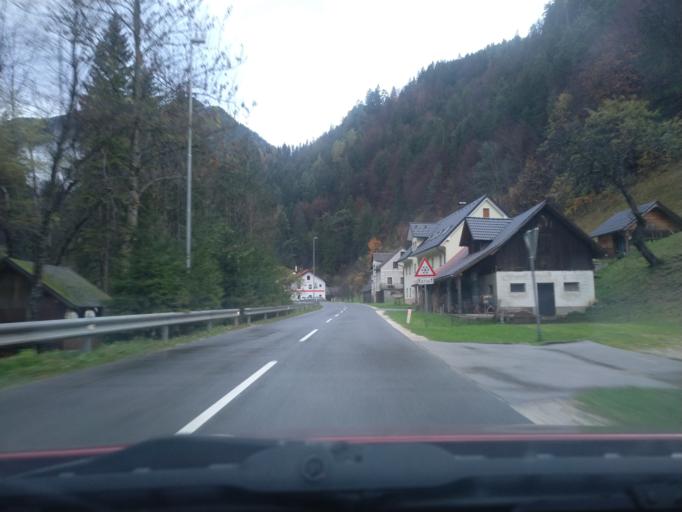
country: SI
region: Solcava
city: Solcava
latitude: 46.4178
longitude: 14.6977
